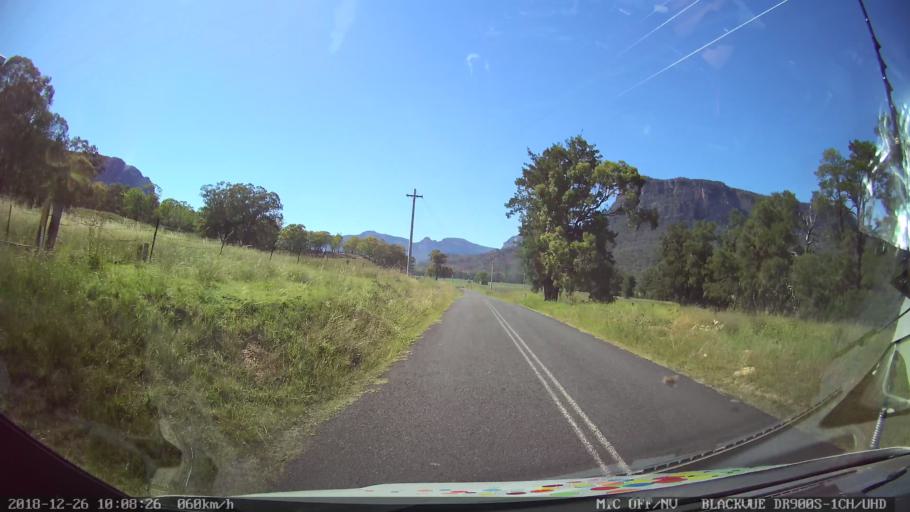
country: AU
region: New South Wales
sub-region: Mid-Western Regional
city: Kandos
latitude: -33.0975
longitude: 150.2303
